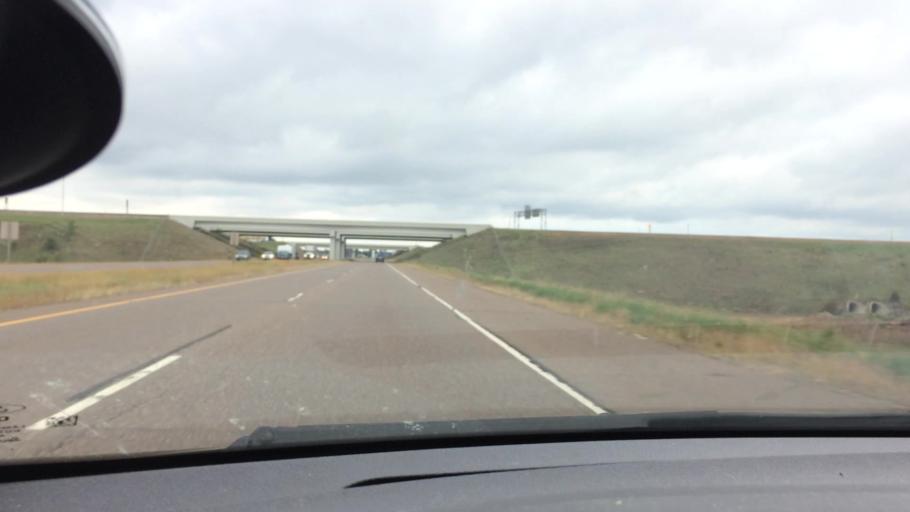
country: US
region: Wisconsin
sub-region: Chippewa County
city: Lake Hallie
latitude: 44.8900
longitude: -91.4194
